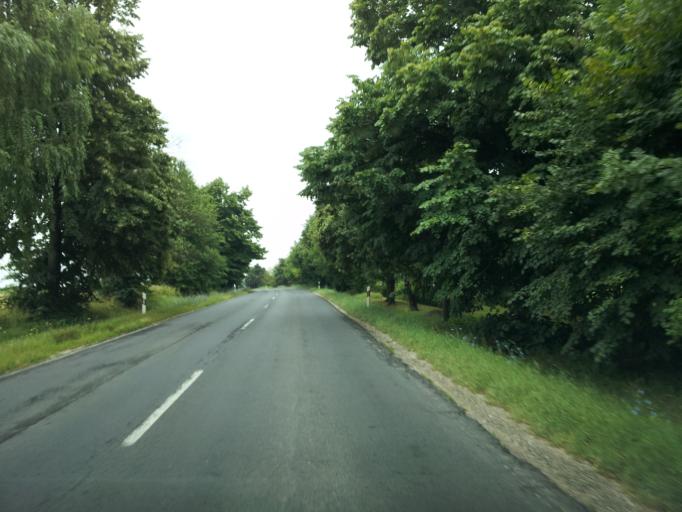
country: HU
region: Vas
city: Kormend
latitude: 46.9725
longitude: 16.6347
